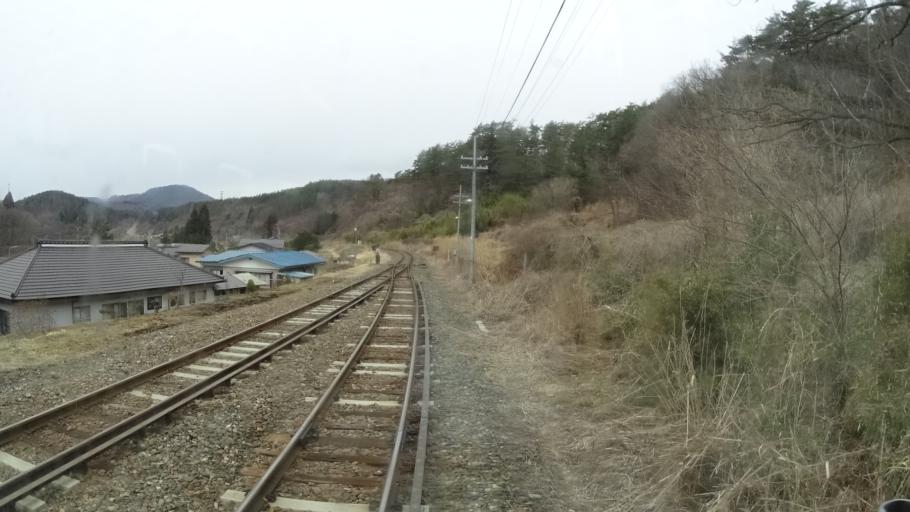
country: JP
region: Iwate
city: Tono
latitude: 39.3521
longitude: 141.3501
